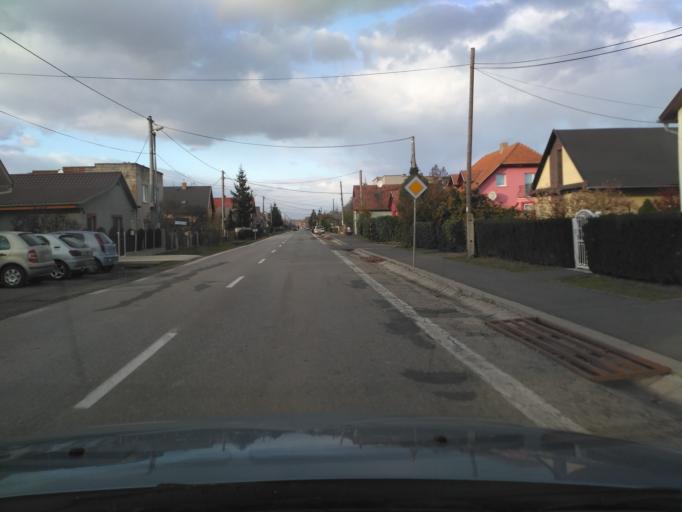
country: HU
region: Borsod-Abauj-Zemplen
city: Satoraljaujhely
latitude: 48.4039
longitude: 21.6688
